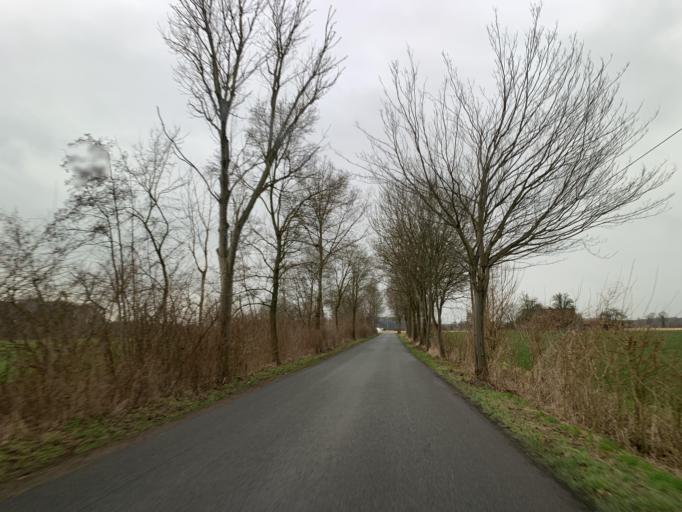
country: DE
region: North Rhine-Westphalia
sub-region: Regierungsbezirk Munster
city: Senden
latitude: 51.8786
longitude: 7.4618
